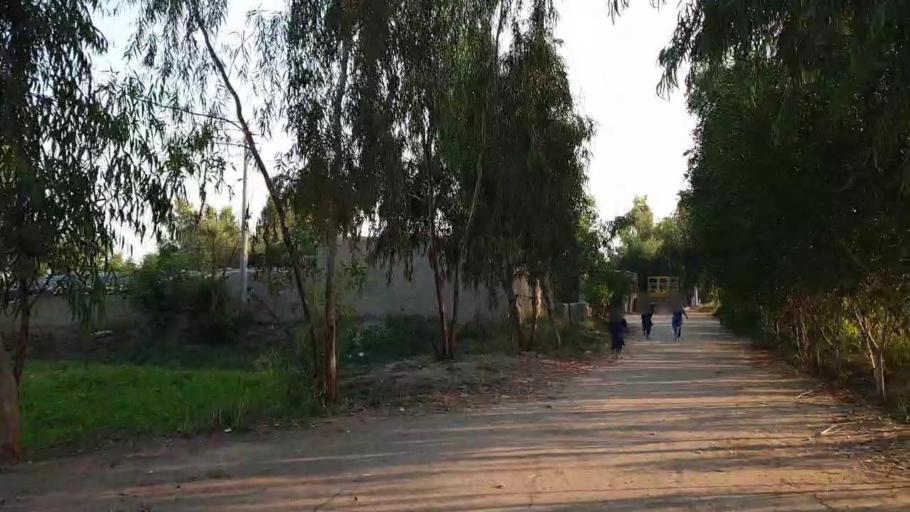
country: PK
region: Sindh
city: Sehwan
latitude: 26.4431
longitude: 67.7799
